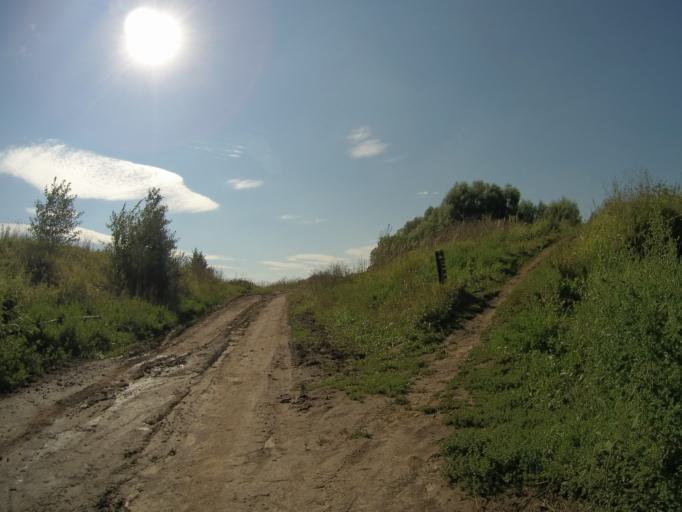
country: RU
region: Vladimir
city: Bogolyubovo
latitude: 56.2614
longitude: 40.5379
